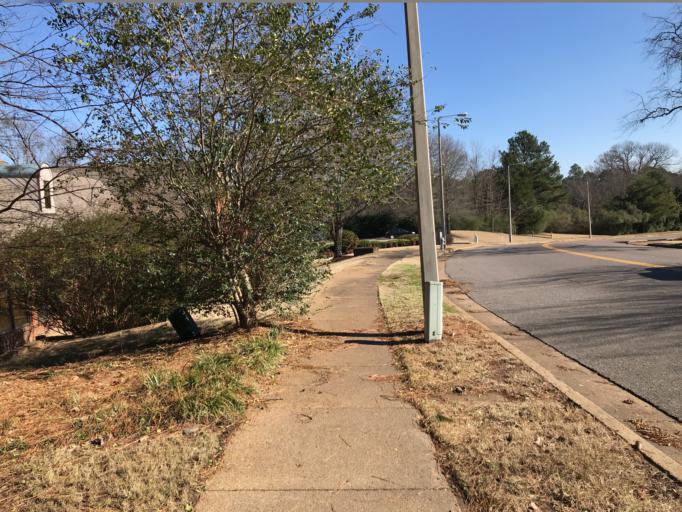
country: US
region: Tennessee
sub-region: Shelby County
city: Germantown
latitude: 35.1106
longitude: -89.8667
